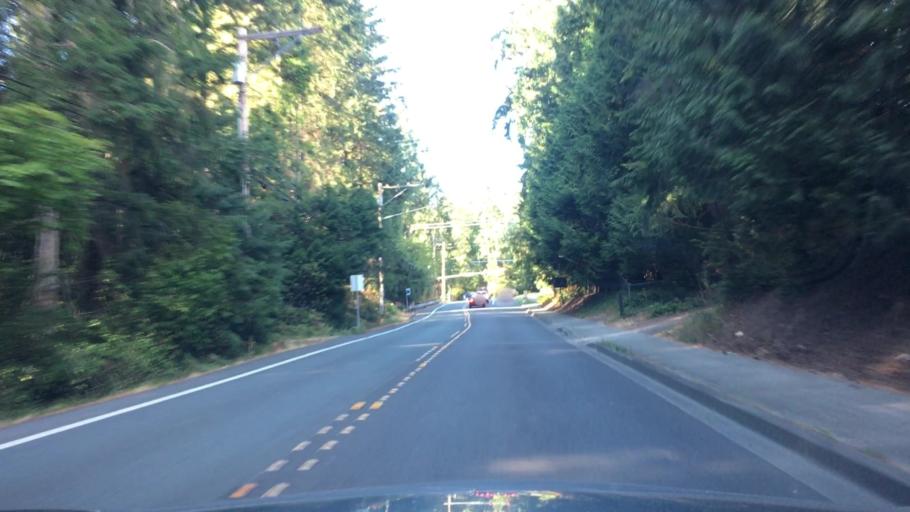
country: US
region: Washington
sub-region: Snohomish County
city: North Creek
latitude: 47.7897
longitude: -122.1864
